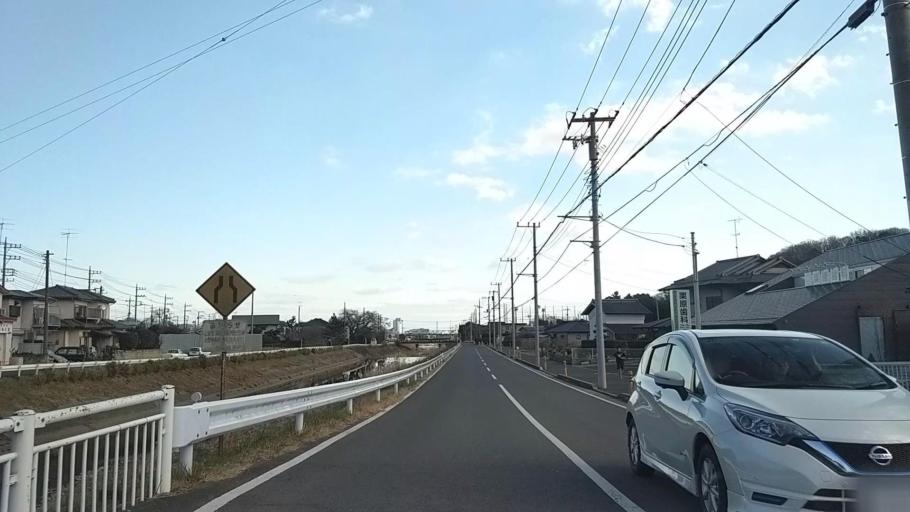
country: JP
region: Kanagawa
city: Atsugi
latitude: 35.4342
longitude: 139.3163
